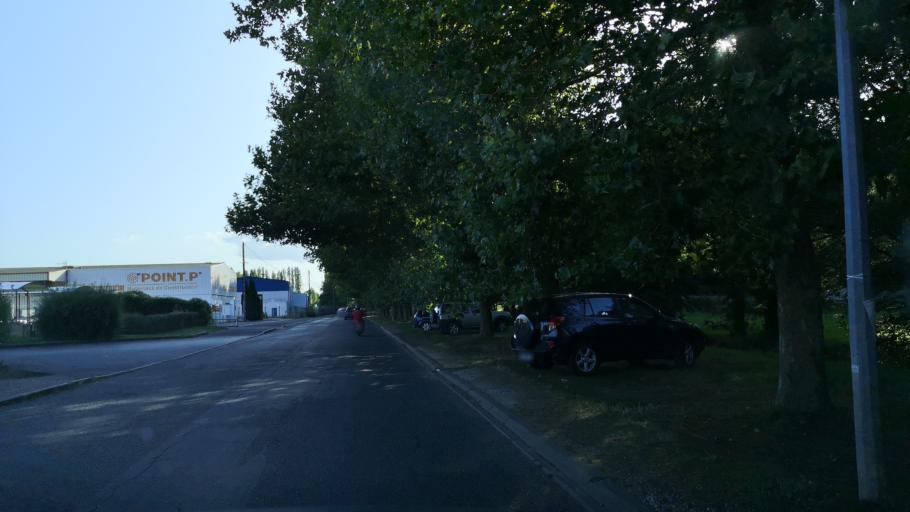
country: FR
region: Centre
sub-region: Departement d'Indre-et-Loire
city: Langeais
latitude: 47.3329
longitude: 0.4246
